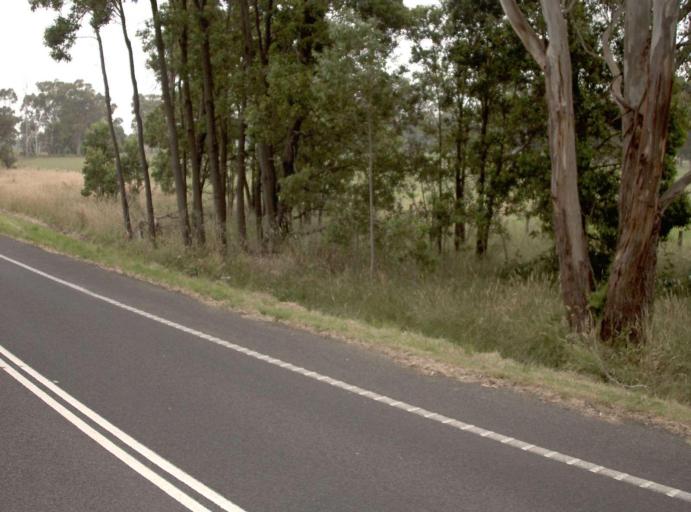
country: AU
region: Victoria
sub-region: Latrobe
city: Morwell
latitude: -38.2820
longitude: 146.3207
